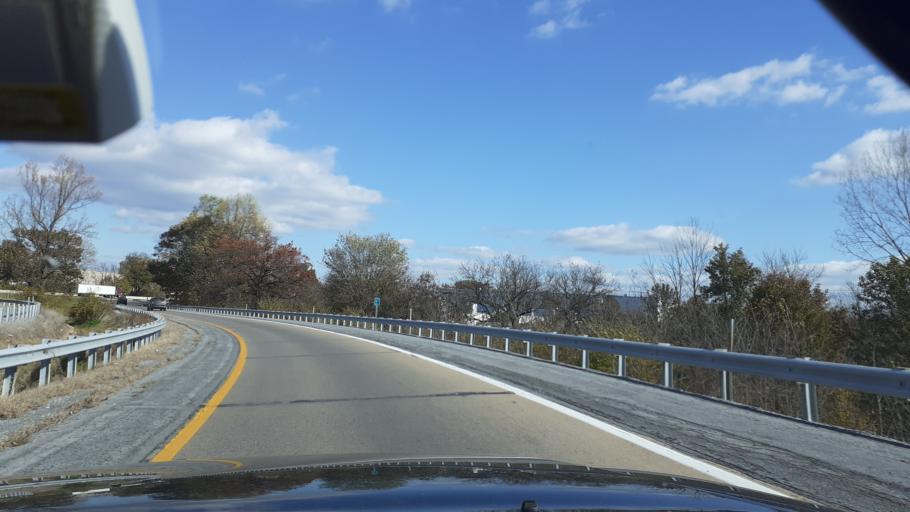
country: US
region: West Virginia
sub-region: Berkeley County
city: Martinsburg
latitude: 39.4951
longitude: -77.9570
